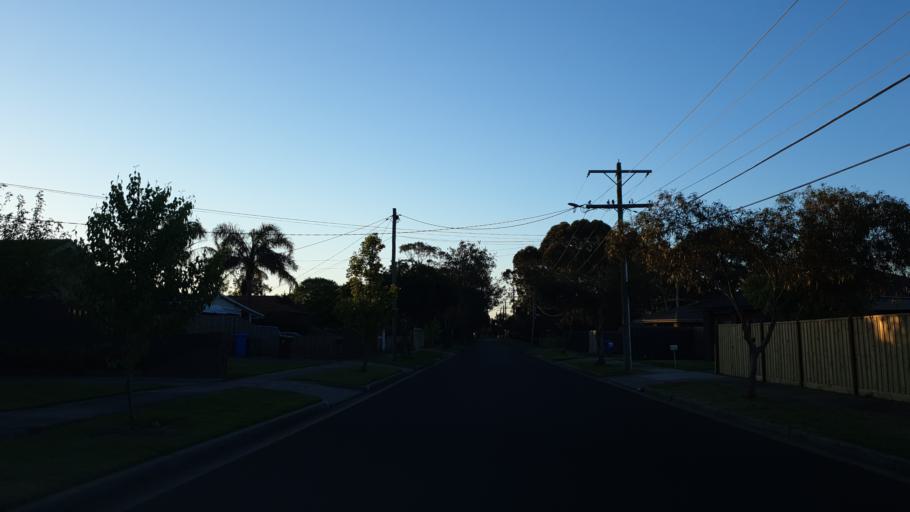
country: AU
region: Victoria
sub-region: Casey
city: Cranbourne
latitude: -38.1035
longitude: 145.2881
